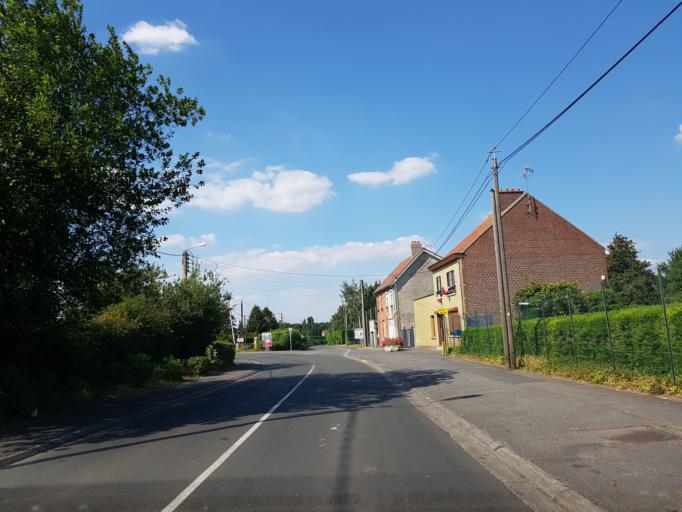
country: FR
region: Nord-Pas-de-Calais
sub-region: Departement du Nord
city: Lourches
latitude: 50.3185
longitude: 3.3427
